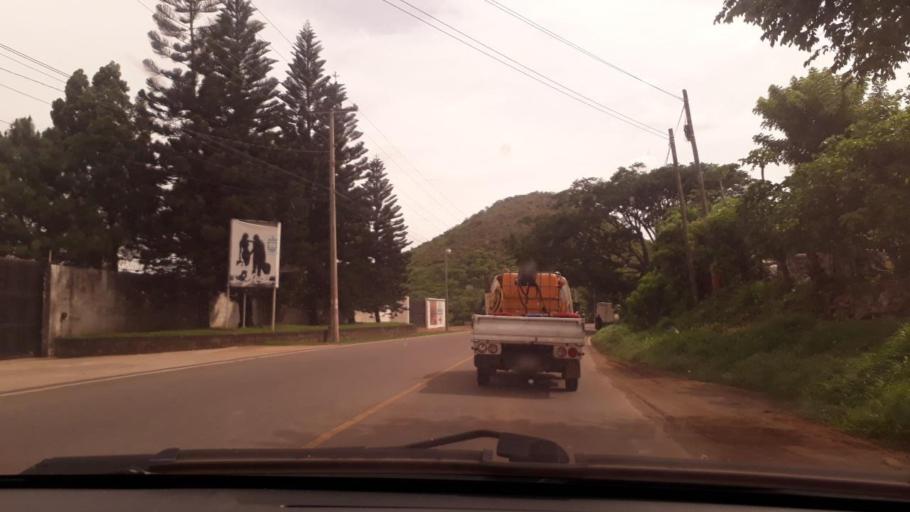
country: GT
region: Jutiapa
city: Jutiapa
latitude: 14.3018
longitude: -89.8729
